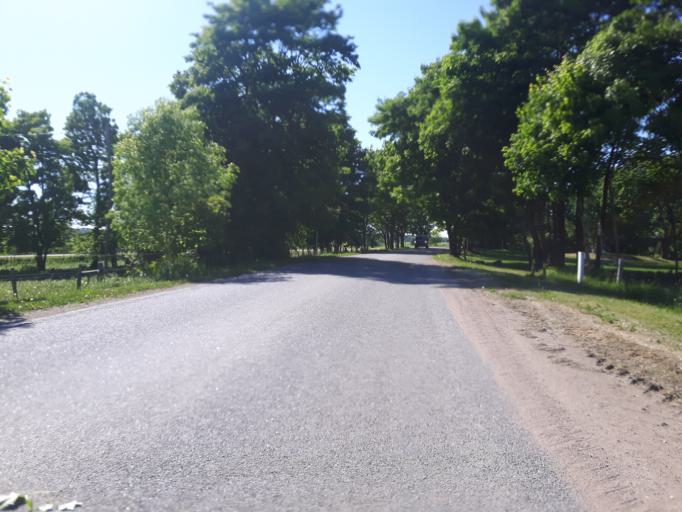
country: EE
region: Laeaene-Virumaa
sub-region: Haljala vald
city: Haljala
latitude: 59.5424
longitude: 26.1513
